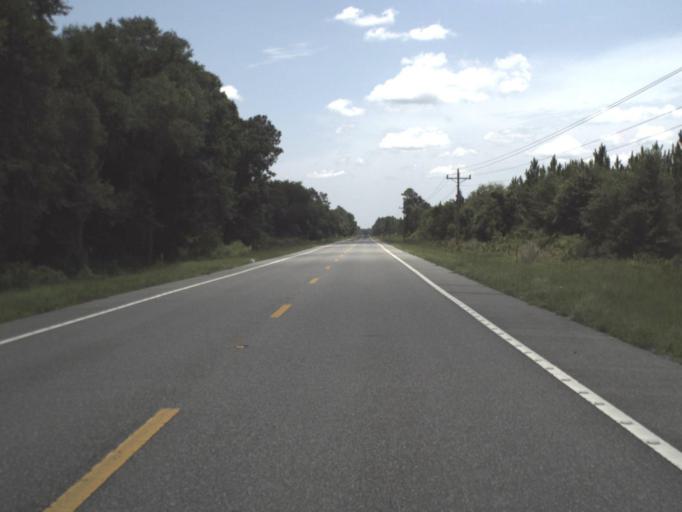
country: US
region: Florida
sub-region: Taylor County
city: Steinhatchee
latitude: 29.7633
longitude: -83.3442
